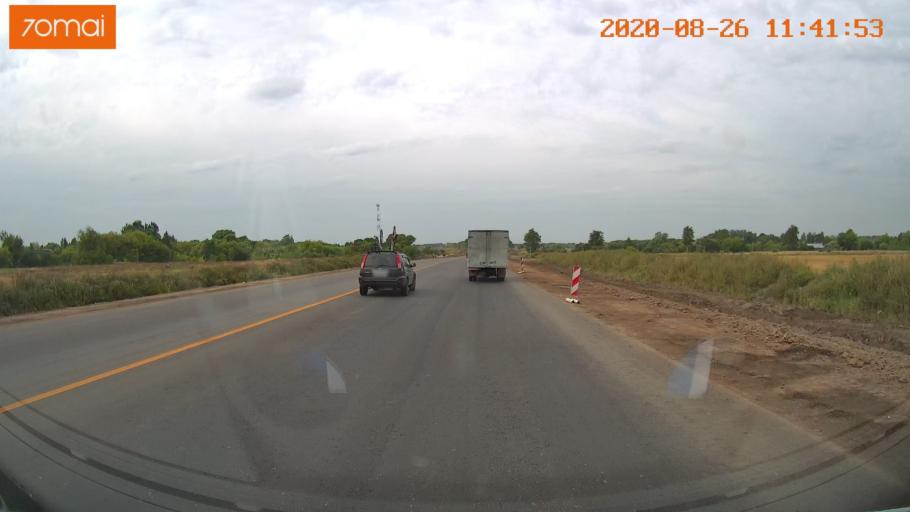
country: RU
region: Rjazan
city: Shilovo
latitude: 54.2960
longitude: 40.7025
